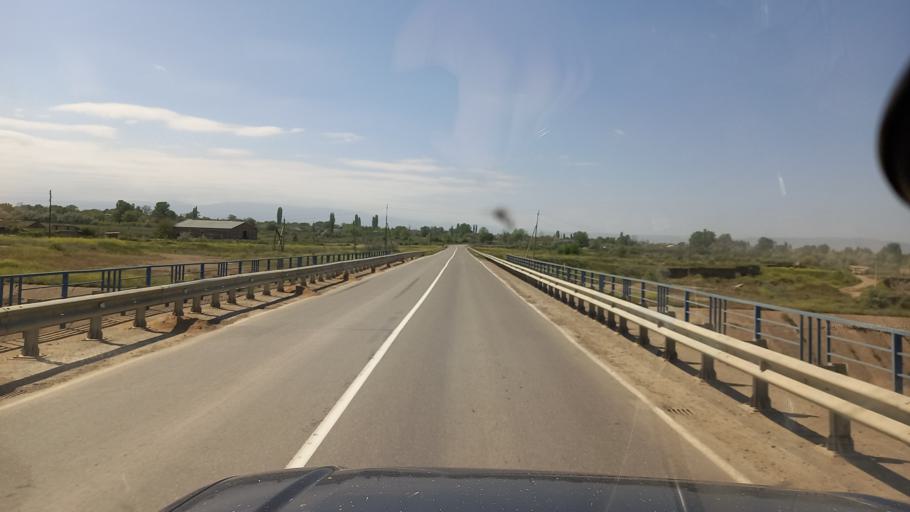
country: RU
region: Dagestan
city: Novaya Maka
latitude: 41.8090
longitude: 48.4107
